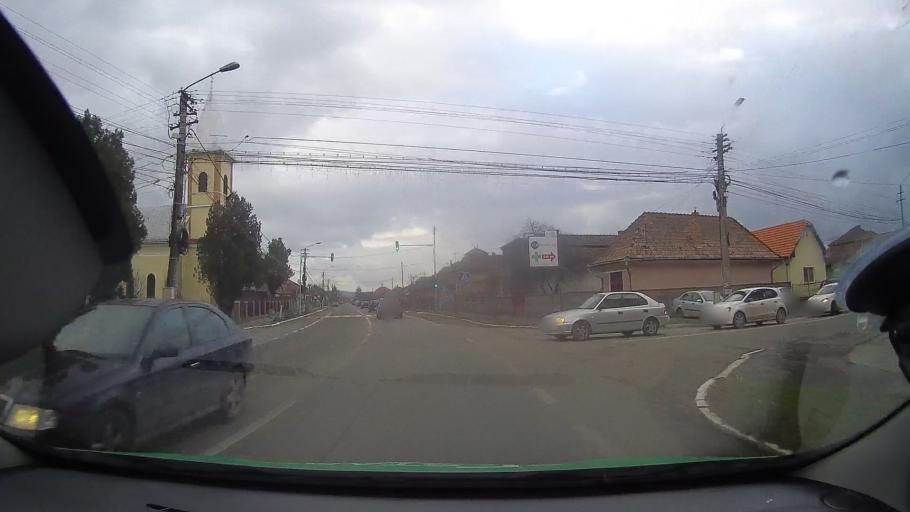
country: RO
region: Cluj
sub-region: Municipiul Campia Turzii
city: Campia Turzii
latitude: 46.5354
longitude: 23.8958
